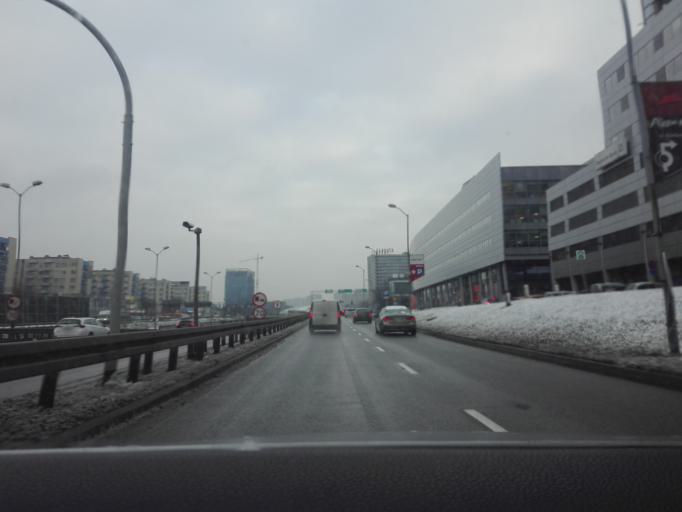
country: PL
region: Silesian Voivodeship
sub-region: Katowice
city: Katowice
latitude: 50.2660
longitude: 19.0155
